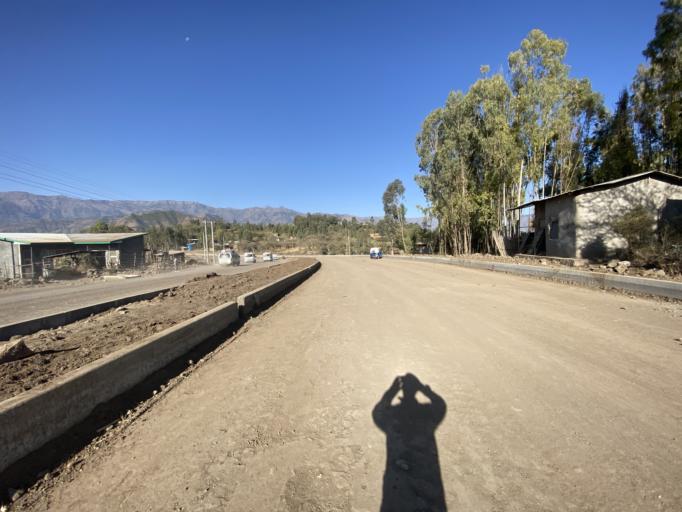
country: ET
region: Amhara
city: Robit
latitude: 11.8278
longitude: 39.5694
